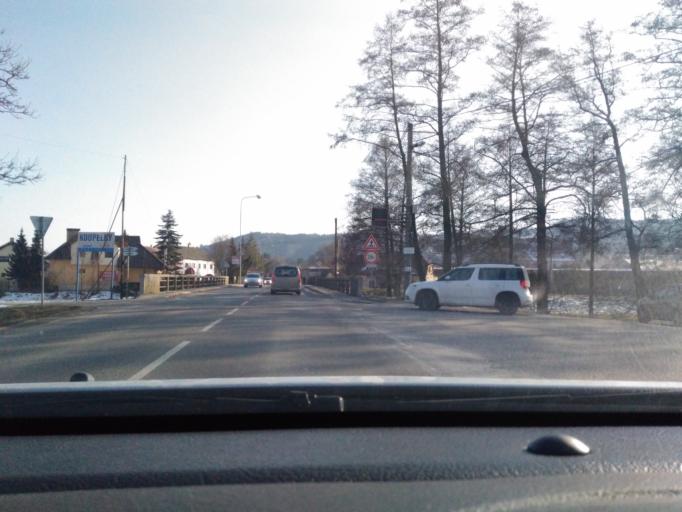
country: CZ
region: South Moravian
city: Predklasteri
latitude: 49.3568
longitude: 16.4010
